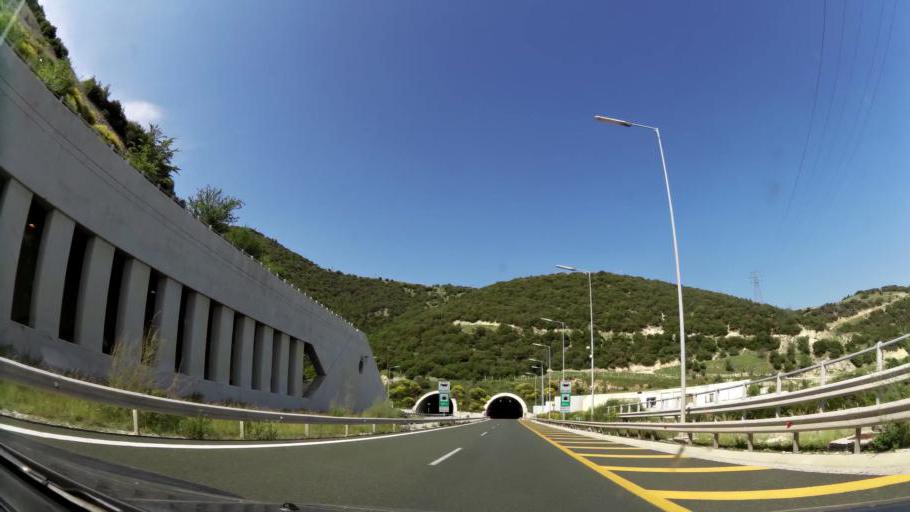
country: GR
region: West Macedonia
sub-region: Nomos Kozanis
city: Velventos
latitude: 40.3736
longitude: 22.0847
